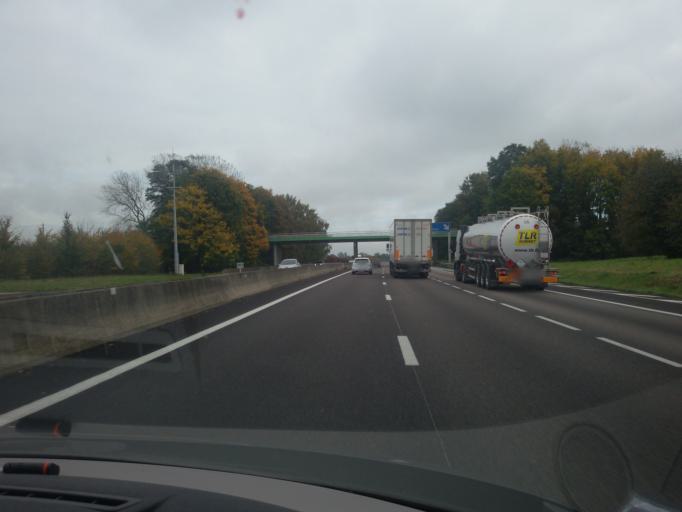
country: FR
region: Haute-Normandie
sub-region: Departement de l'Eure
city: Hauville
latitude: 49.3720
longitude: 0.6822
